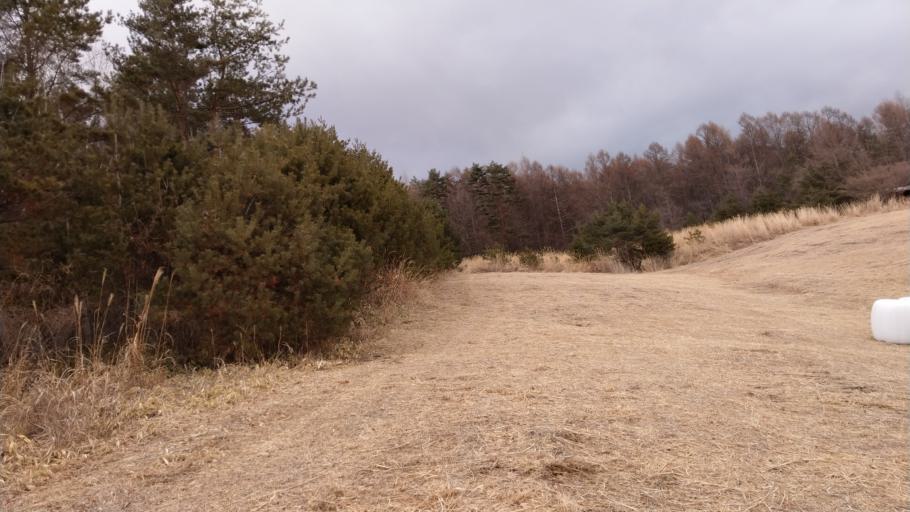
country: JP
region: Nagano
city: Komoro
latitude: 36.3678
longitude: 138.4379
